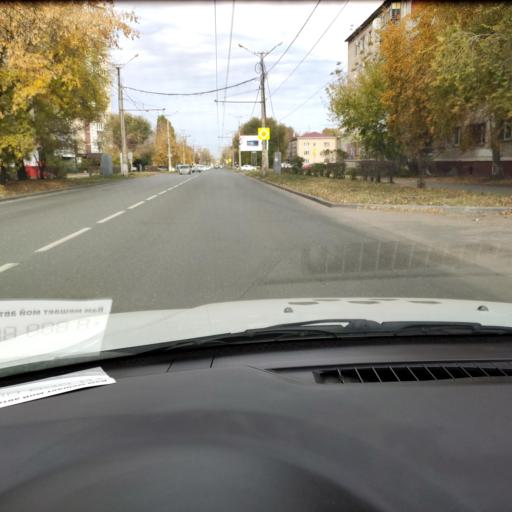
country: RU
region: Samara
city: Tol'yatti
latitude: 53.5269
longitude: 49.4133
